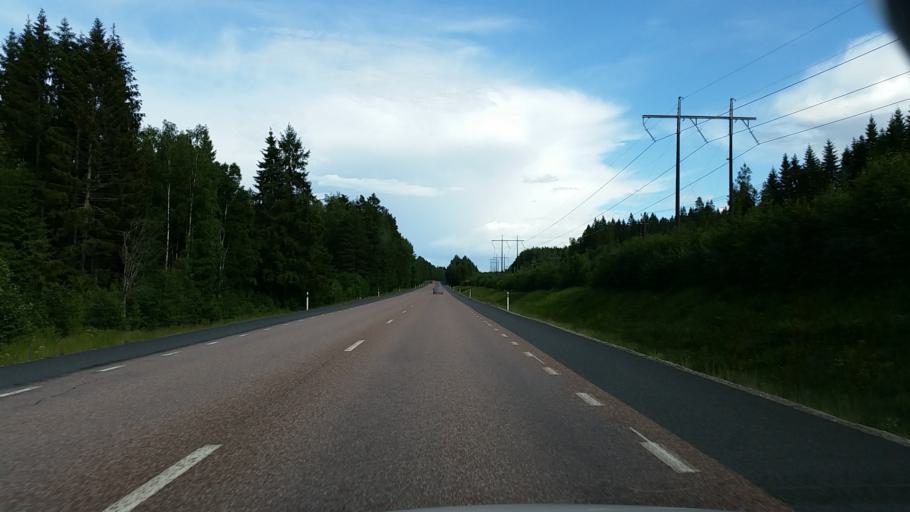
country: SE
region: Dalarna
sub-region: Smedjebackens Kommun
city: Smedjebacken
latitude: 60.0363
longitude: 15.5841
